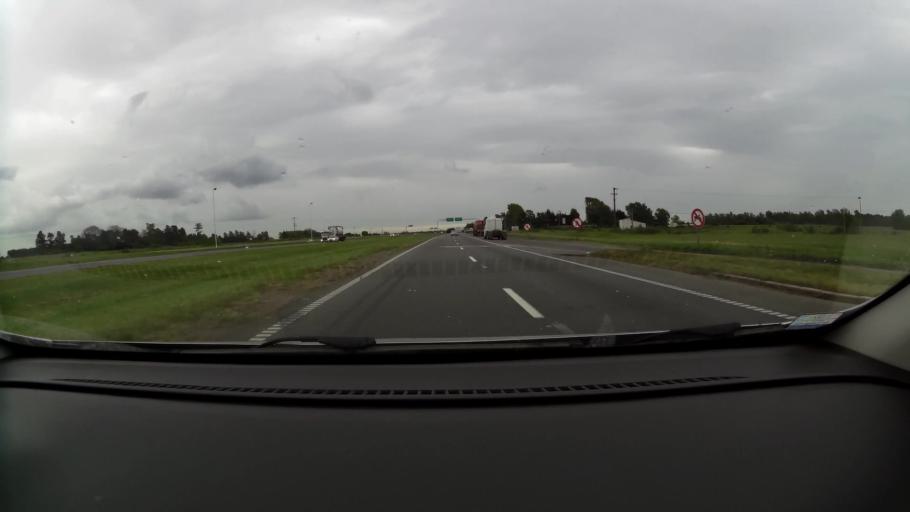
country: AR
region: Buenos Aires
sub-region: Partido de Baradero
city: Baradero
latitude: -33.8541
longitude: -59.5453
